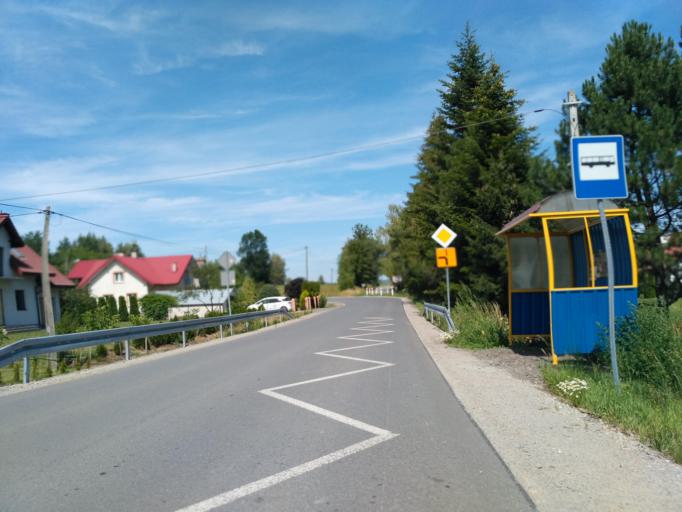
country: PL
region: Subcarpathian Voivodeship
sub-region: Powiat sanocki
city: Strachocina
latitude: 49.5782
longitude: 22.1222
